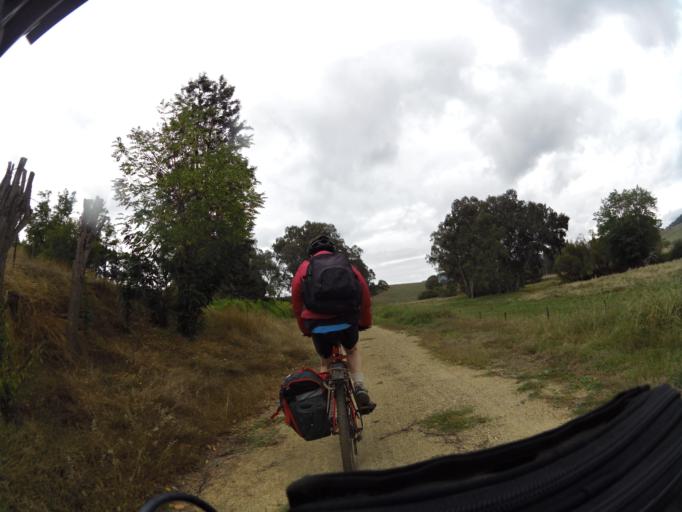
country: AU
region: New South Wales
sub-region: Albury Municipality
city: East Albury
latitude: -36.1947
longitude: 147.3088
